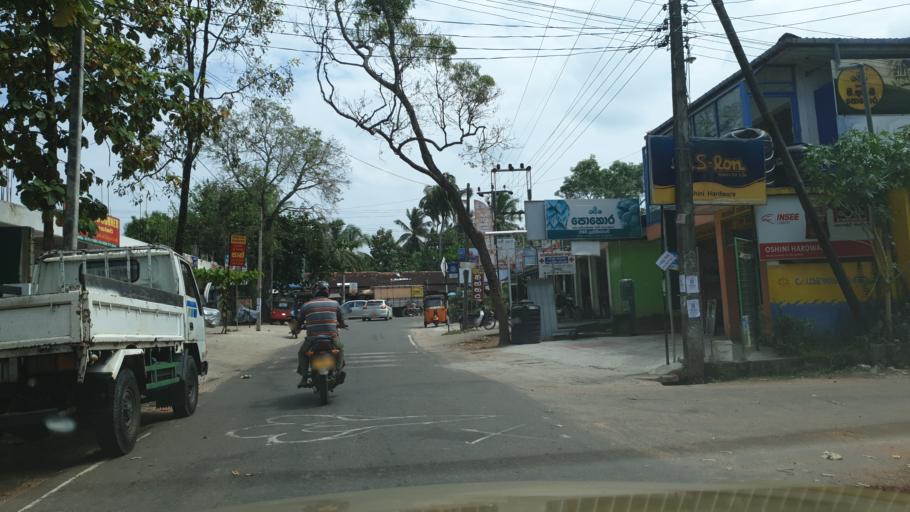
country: LK
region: North Western
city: Kuliyapitiya
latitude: 7.3475
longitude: 79.9841
